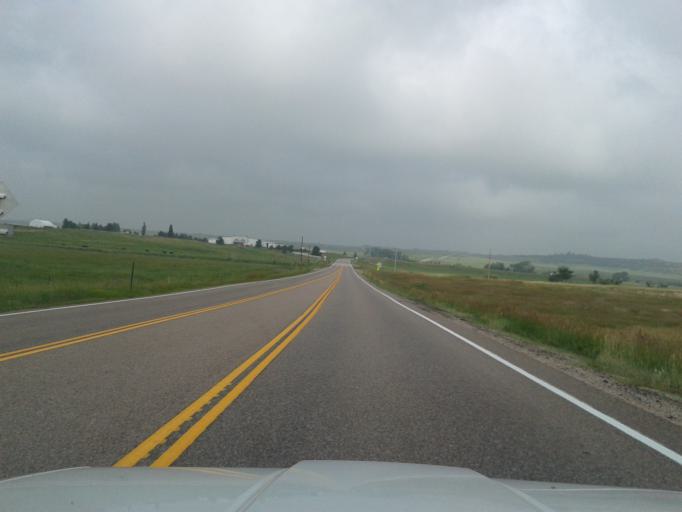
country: US
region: Colorado
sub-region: Elbert County
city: Elizabeth
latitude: 39.2618
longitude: -104.7057
